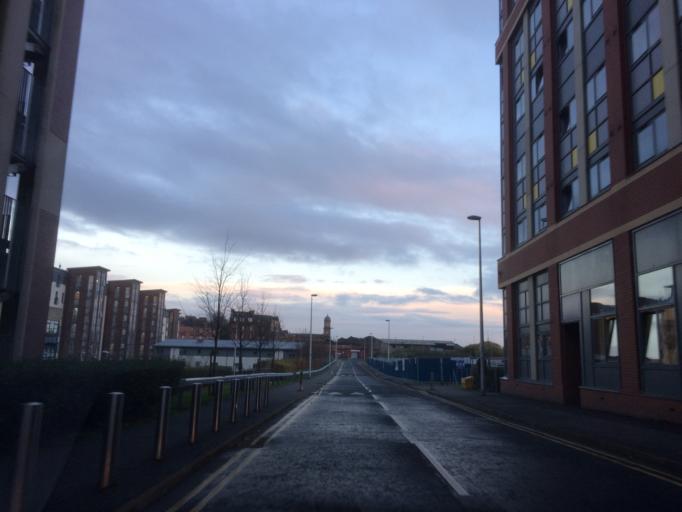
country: GB
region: Scotland
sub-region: Glasgow City
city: Glasgow
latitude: 55.8592
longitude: -4.2368
